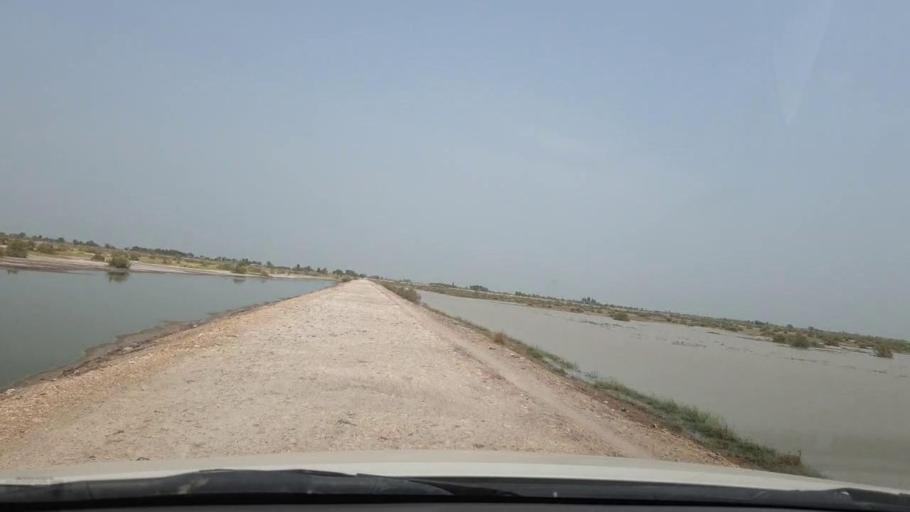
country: PK
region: Sindh
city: Rustam jo Goth
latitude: 28.0677
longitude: 68.8172
